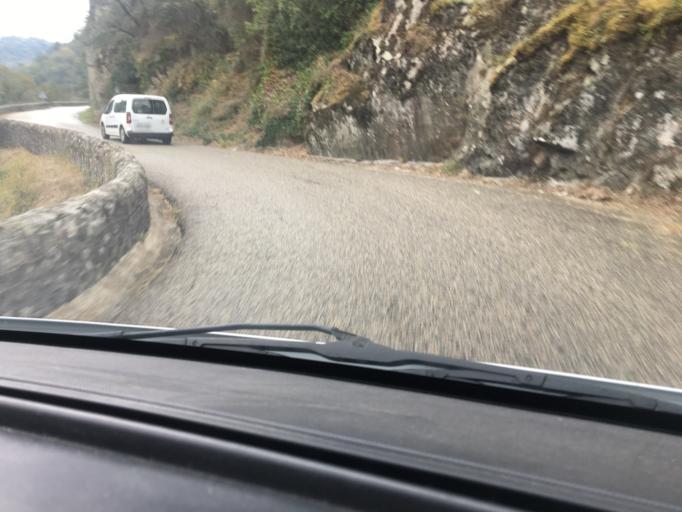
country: FR
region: Rhone-Alpes
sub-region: Departement de l'Ardeche
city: Saint-Jean-de-Muzols
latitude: 45.0582
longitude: 4.7327
